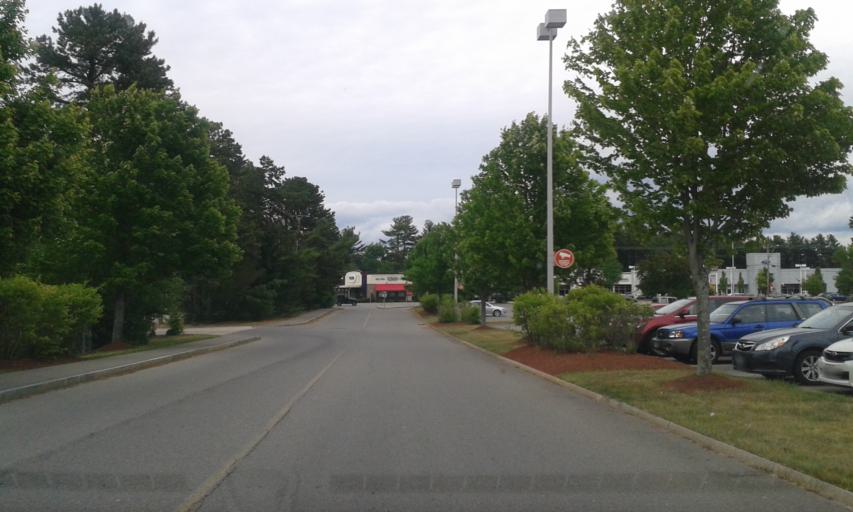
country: US
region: New Hampshire
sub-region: Hillsborough County
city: Litchfield
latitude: 42.7991
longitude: -71.5369
